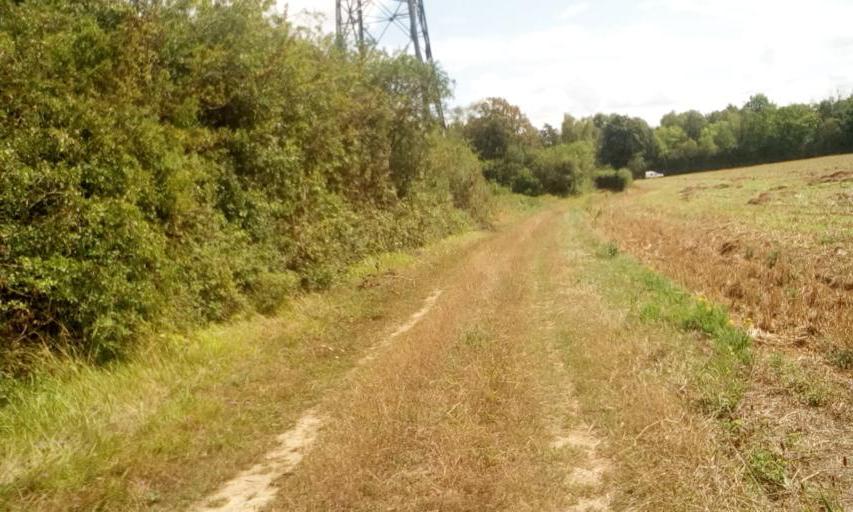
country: FR
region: Lower Normandy
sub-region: Departement du Calvados
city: Cagny
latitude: 49.1099
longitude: -0.2497
